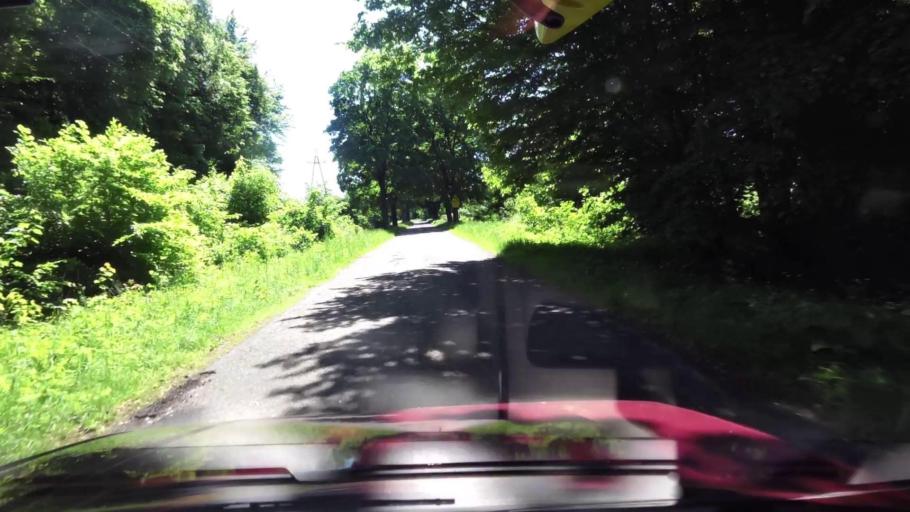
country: PL
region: West Pomeranian Voivodeship
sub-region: Powiat koszalinski
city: Bobolice
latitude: 54.0251
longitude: 16.6412
